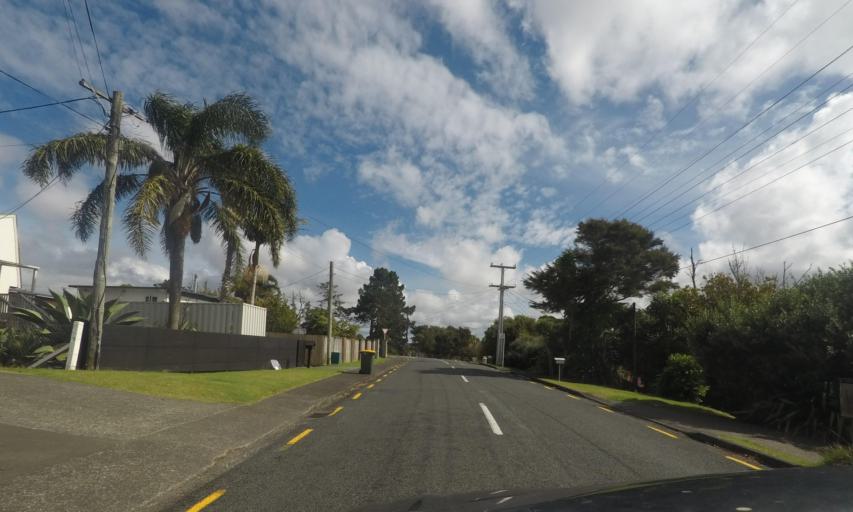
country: NZ
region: Auckland
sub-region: Auckland
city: Rosebank
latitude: -36.7807
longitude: 174.6515
